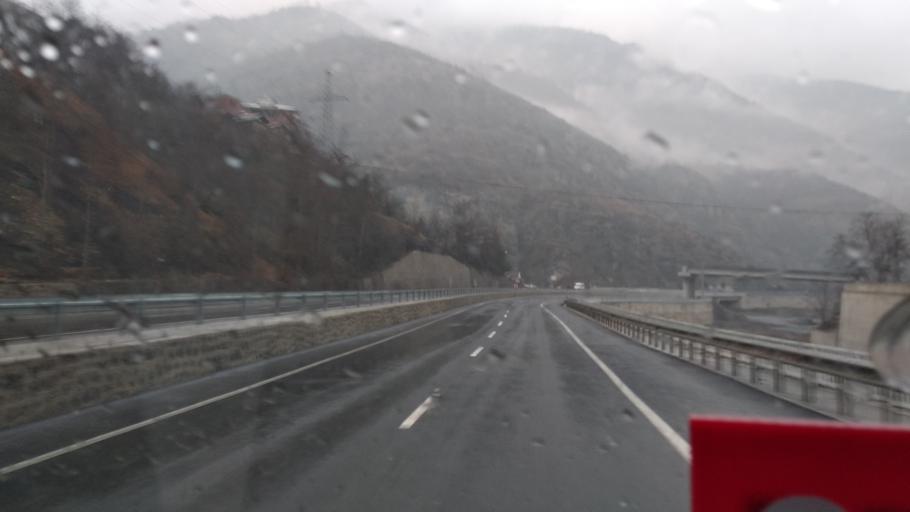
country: TR
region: Trabzon
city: Macka
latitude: 40.7979
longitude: 39.5845
